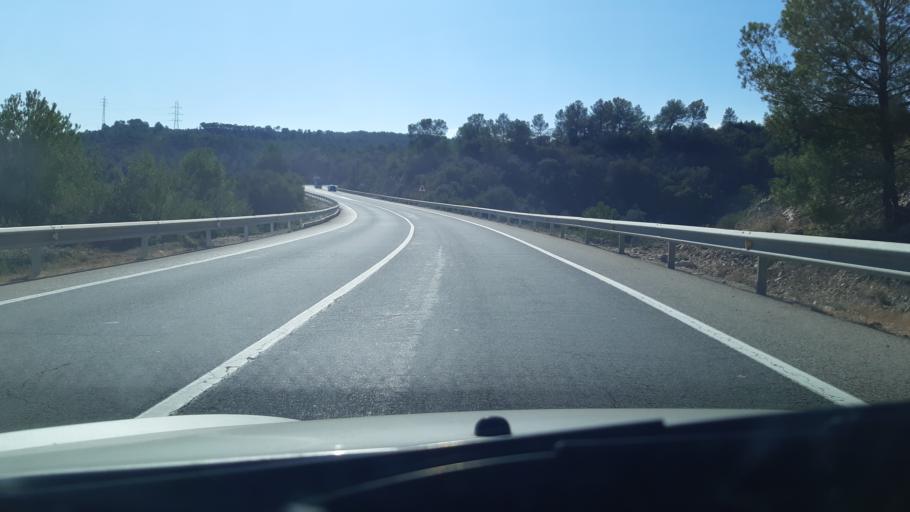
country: ES
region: Catalonia
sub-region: Provincia de Tarragona
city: Tivenys
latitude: 40.9347
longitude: 0.4855
